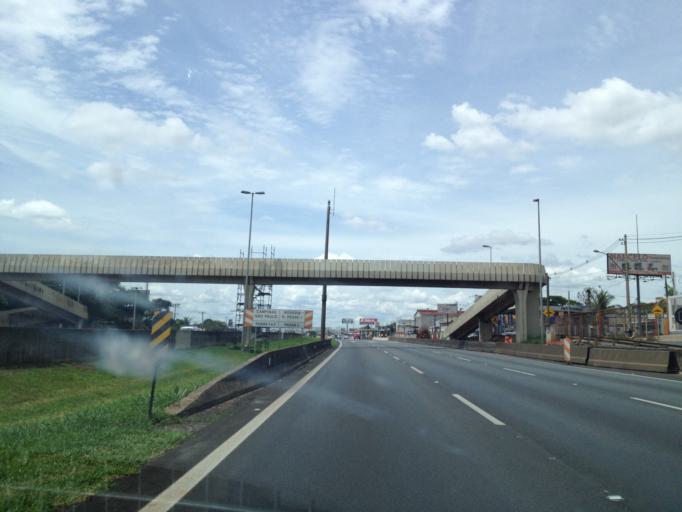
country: BR
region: Sao Paulo
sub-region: Hortolandia
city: Hortolandia
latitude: -22.8467
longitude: -47.1641
